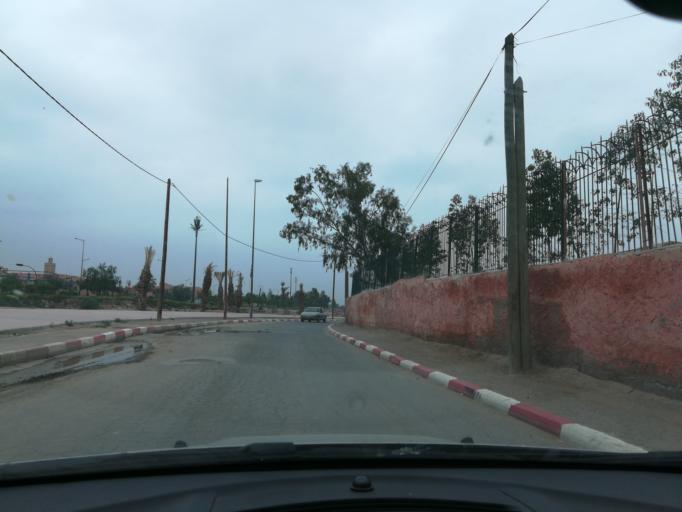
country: MA
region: Marrakech-Tensift-Al Haouz
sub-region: Marrakech
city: Marrakesh
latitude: 31.6490
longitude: -7.9856
